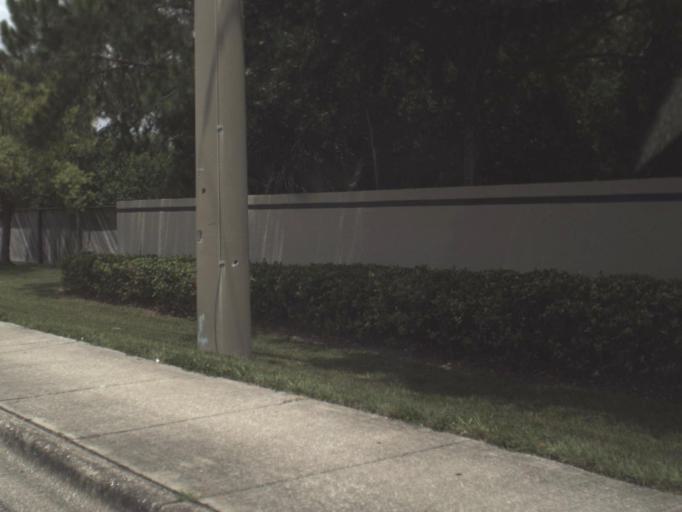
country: US
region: Florida
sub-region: Pinellas County
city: Oldsmar
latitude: 28.0483
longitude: -82.6917
